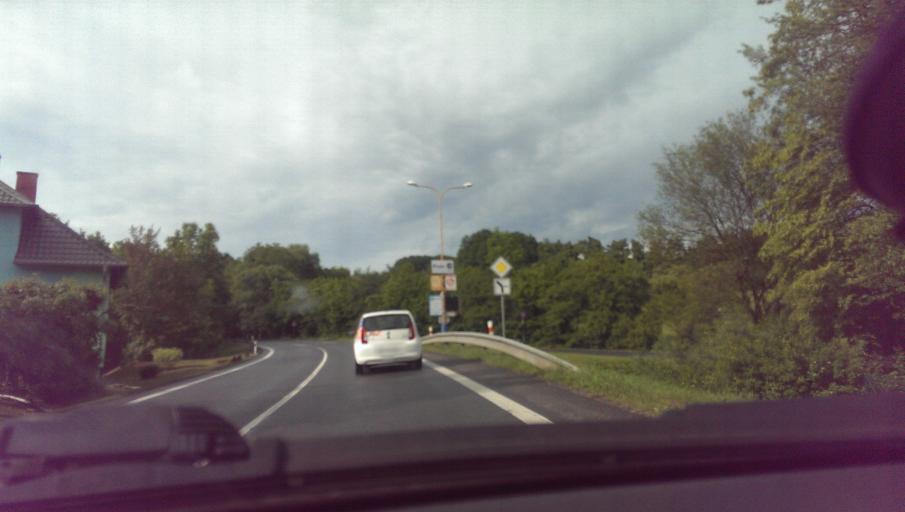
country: CZ
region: Zlin
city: Breznice
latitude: 49.1857
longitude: 17.6571
